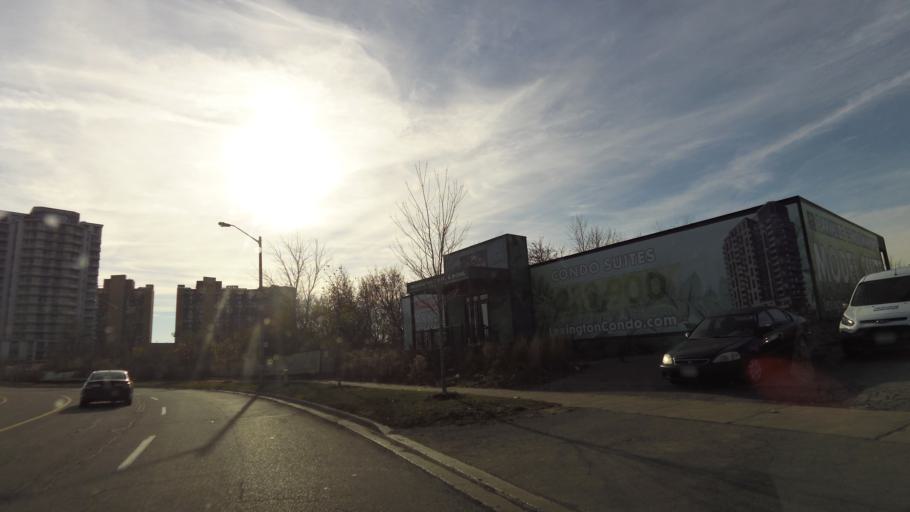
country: CA
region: Ontario
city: Etobicoke
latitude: 43.7224
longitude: -79.6034
